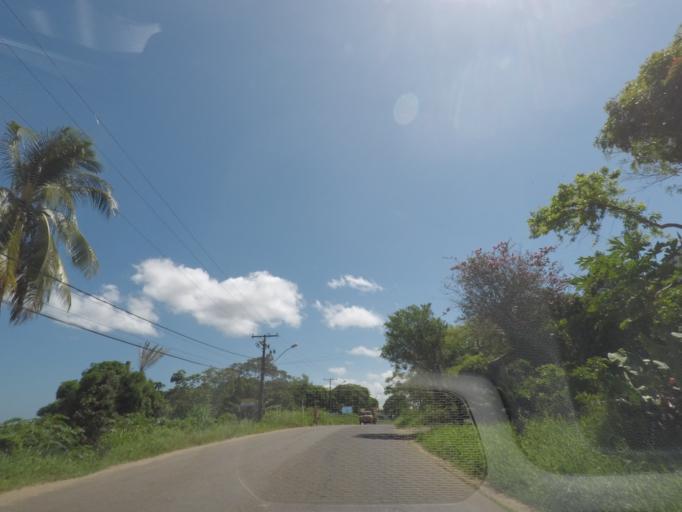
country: BR
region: Bahia
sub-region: Valenca
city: Valenca
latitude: -13.3794
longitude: -39.0743
